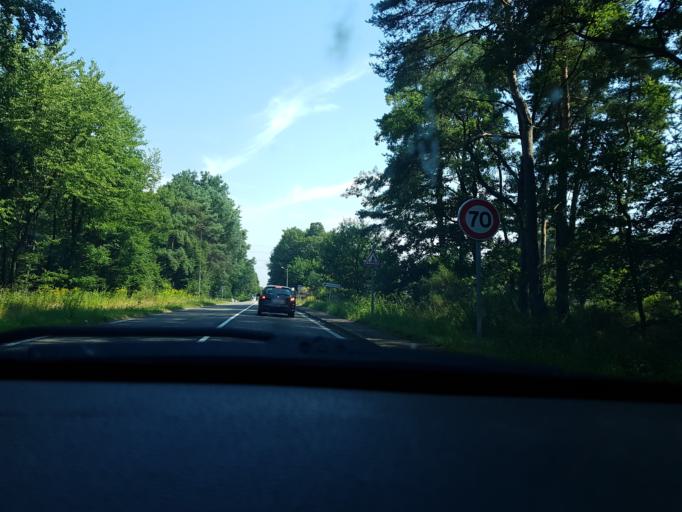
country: FR
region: Lorraine
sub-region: Departement de la Moselle
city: Porcelette
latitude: 49.1663
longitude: 6.6613
